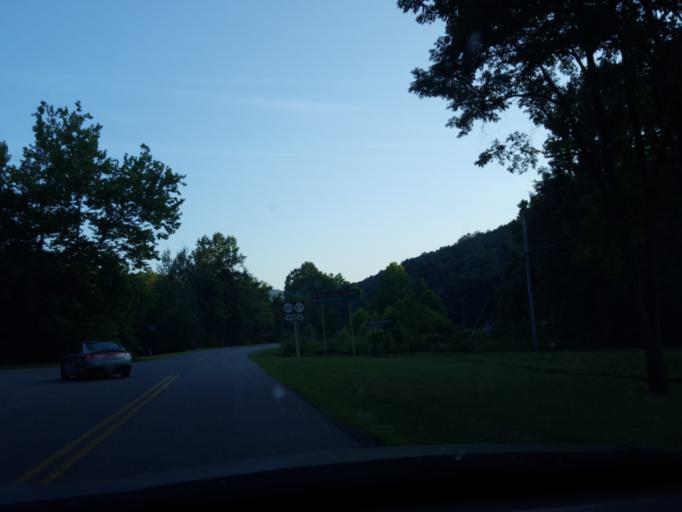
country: US
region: Virginia
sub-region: Augusta County
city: Lyndhurst
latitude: 37.9233
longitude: -78.9856
